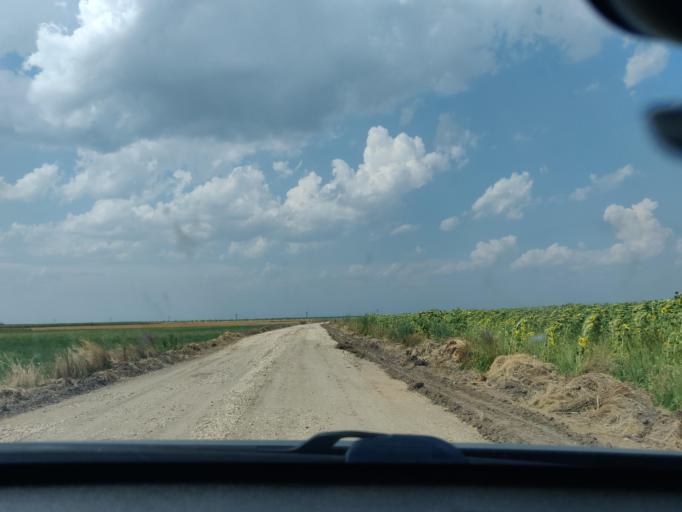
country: RO
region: Teleorman
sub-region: Comuna Sarbeni
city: Sarbeni
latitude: 44.5036
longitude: 25.3974
